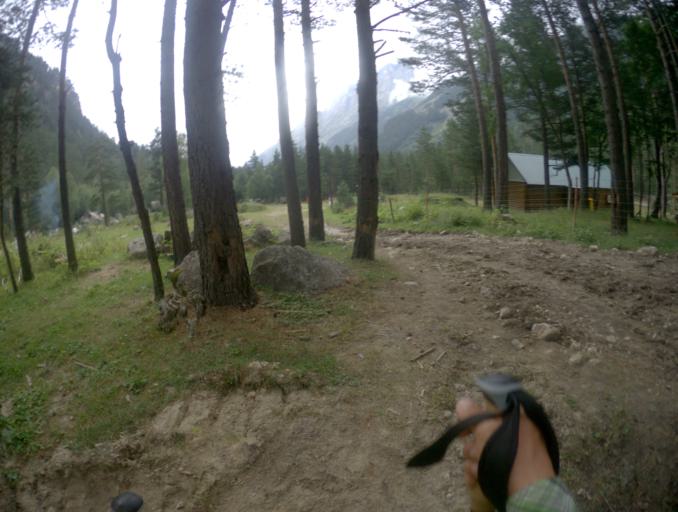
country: RU
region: Karachayevo-Cherkesiya
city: Uchkulan
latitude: 43.2738
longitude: 42.1658
